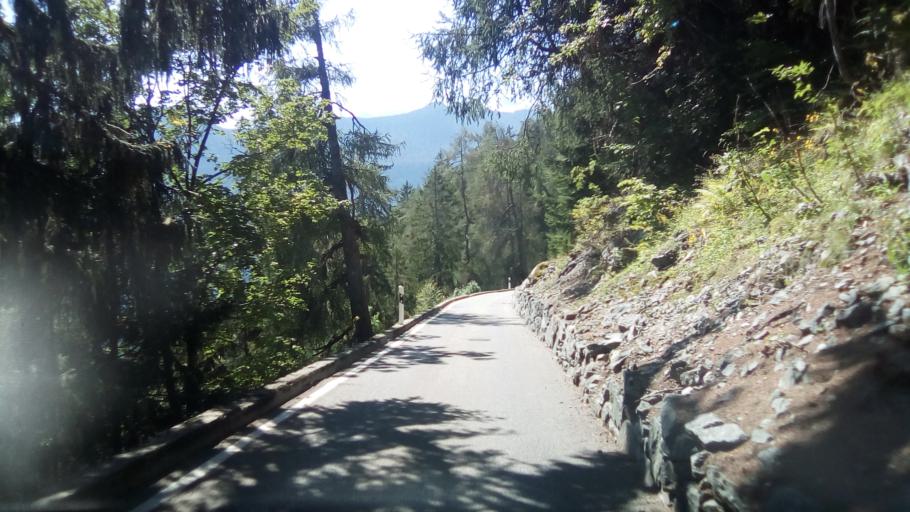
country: CH
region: Valais
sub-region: Saint-Maurice District
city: Salvan
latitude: 46.1347
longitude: 7.0186
